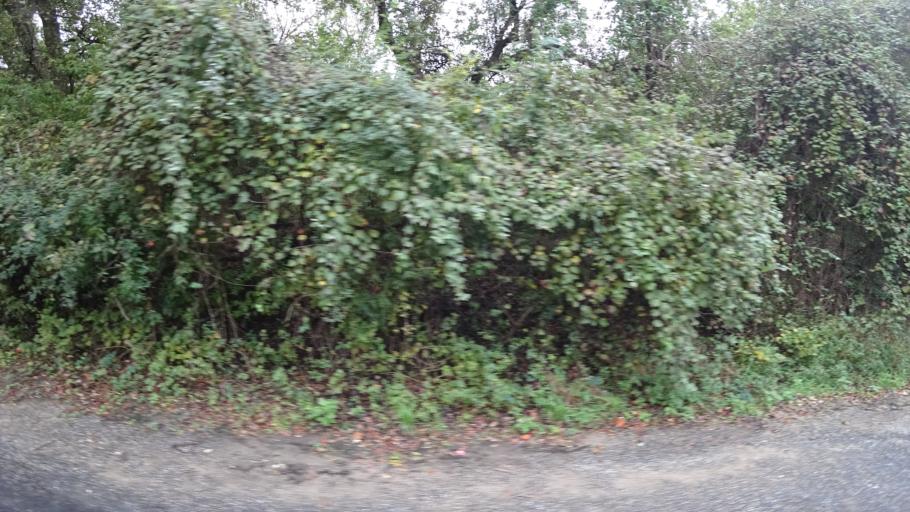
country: US
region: Texas
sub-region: Travis County
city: Rollingwood
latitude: 30.2743
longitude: -97.7747
